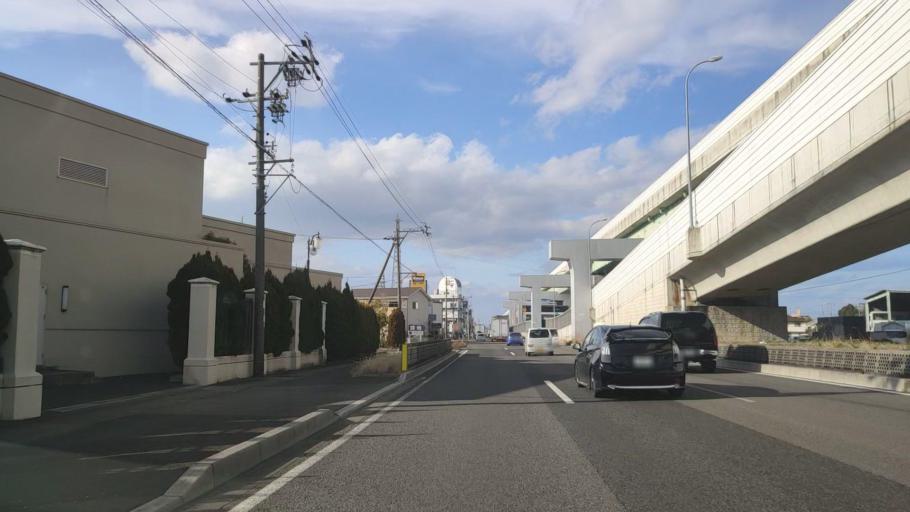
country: JP
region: Aichi
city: Ichinomiya
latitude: 35.2884
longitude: 136.8289
